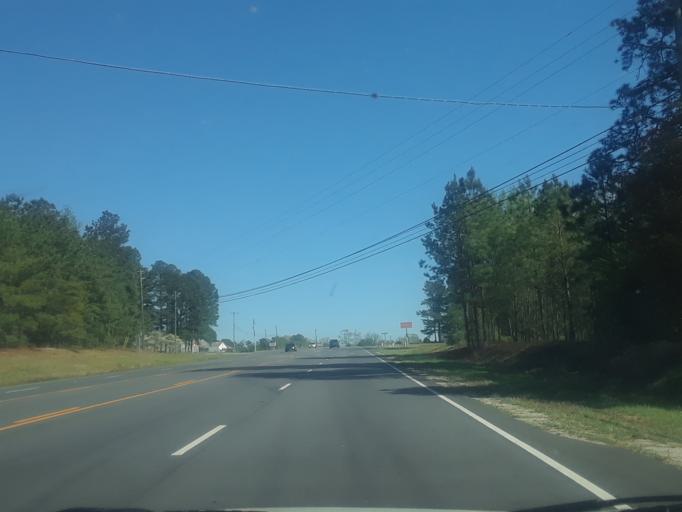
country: US
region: North Carolina
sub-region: Harnett County
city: Buies Creek
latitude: 35.3813
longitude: -78.7172
